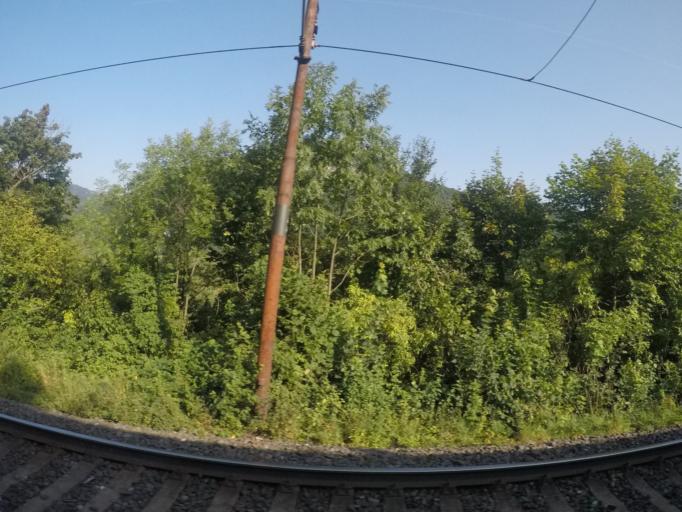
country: SK
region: Presovsky
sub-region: Okres Presov
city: Presov
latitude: 48.8539
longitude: 21.1836
